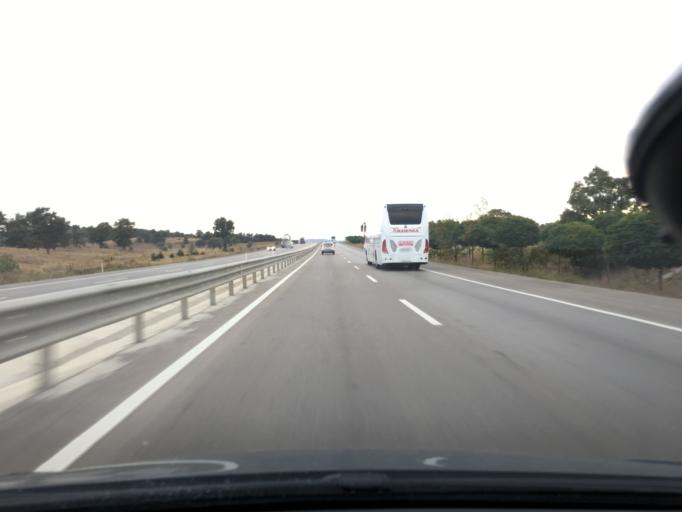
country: TR
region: Afyonkarahisar
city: Sincanli
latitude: 38.6510
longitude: 30.3163
